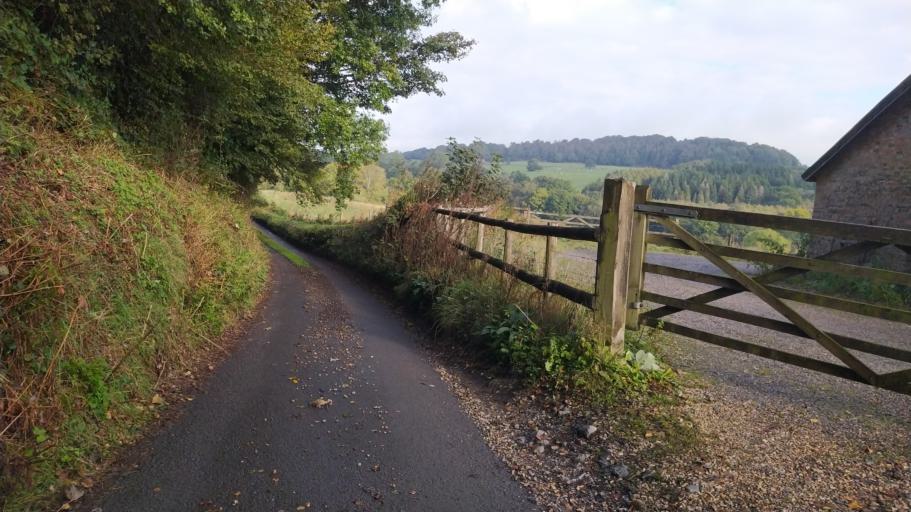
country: GB
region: England
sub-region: Dorset
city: Shaftesbury
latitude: 51.0197
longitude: -2.1340
